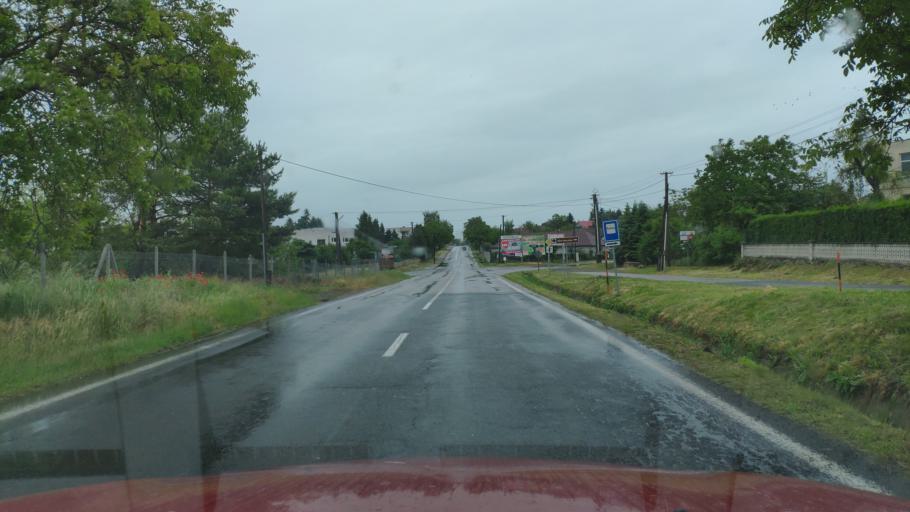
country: HU
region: Borsod-Abauj-Zemplen
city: Ricse
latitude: 48.4317
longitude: 21.9715
